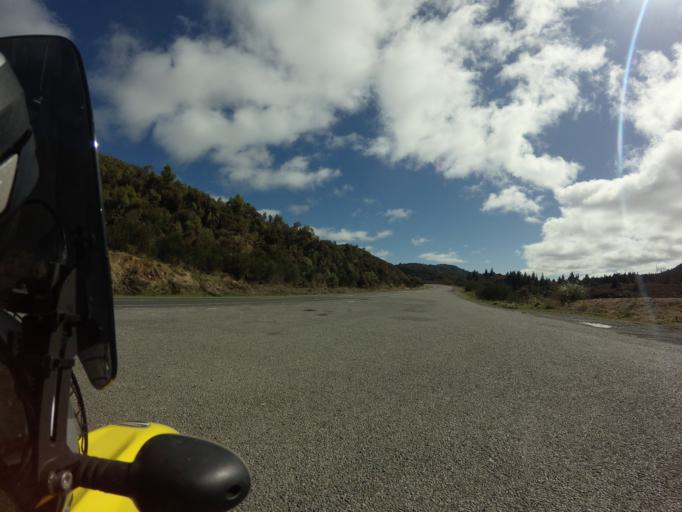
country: NZ
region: Waikato
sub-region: Taupo District
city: Taupo
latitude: -38.9555
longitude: 176.5218
